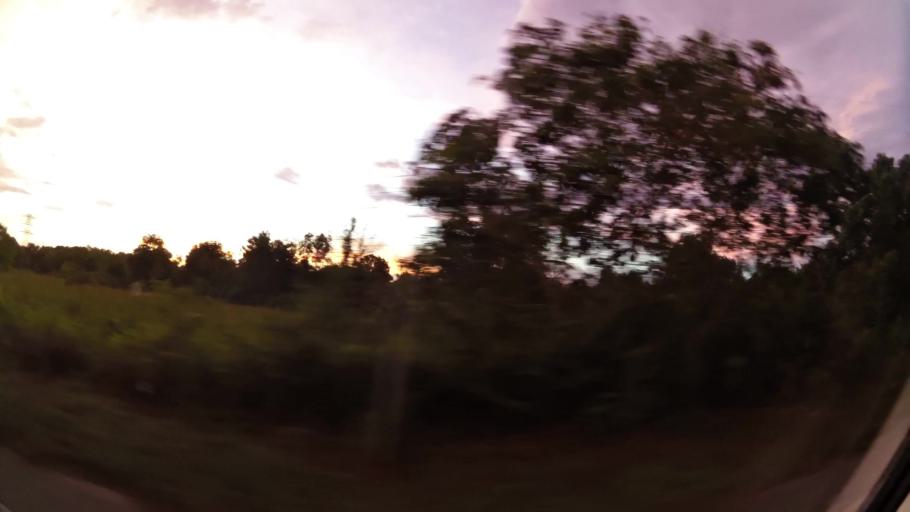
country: BN
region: Belait
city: Seria
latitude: 4.6423
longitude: 114.3984
